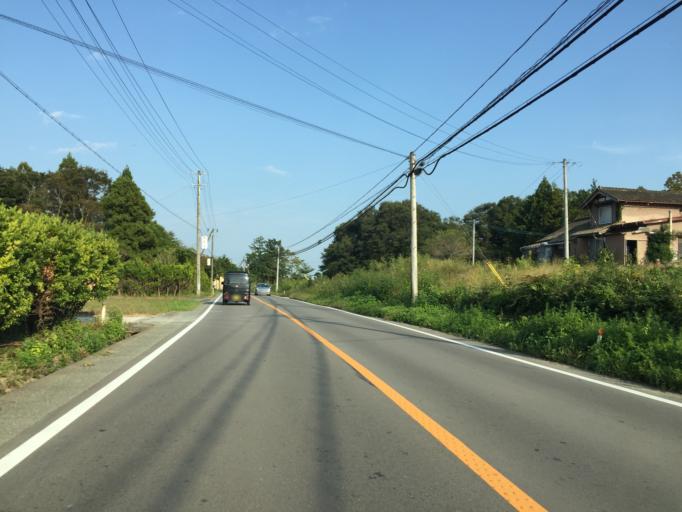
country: JP
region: Fukushima
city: Namie
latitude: 37.4989
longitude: 140.9542
